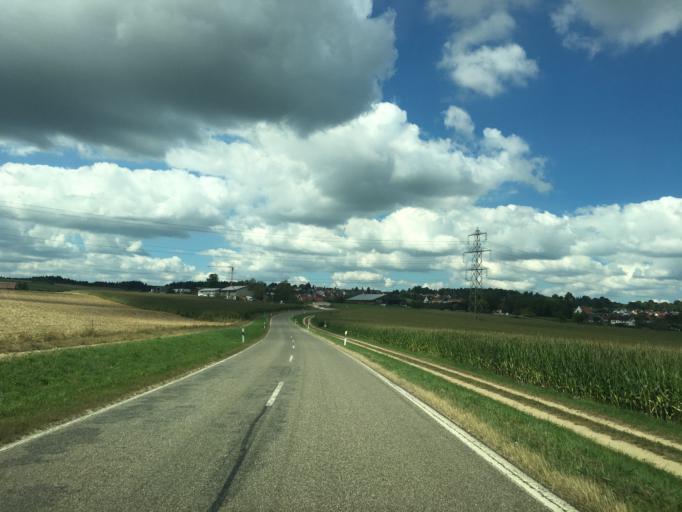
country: DE
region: Baden-Wuerttemberg
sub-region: Tuebingen Region
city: Hayingen
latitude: 48.2709
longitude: 9.4857
